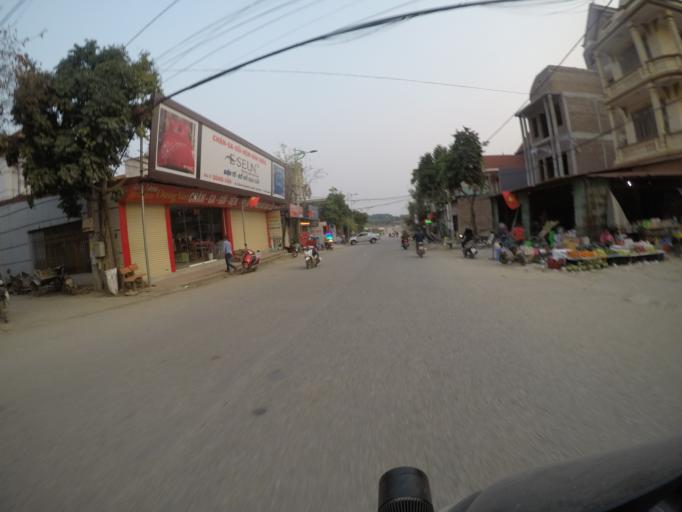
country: VN
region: Vinh Phuc
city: Trai Ngau
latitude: 21.4481
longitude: 105.5721
